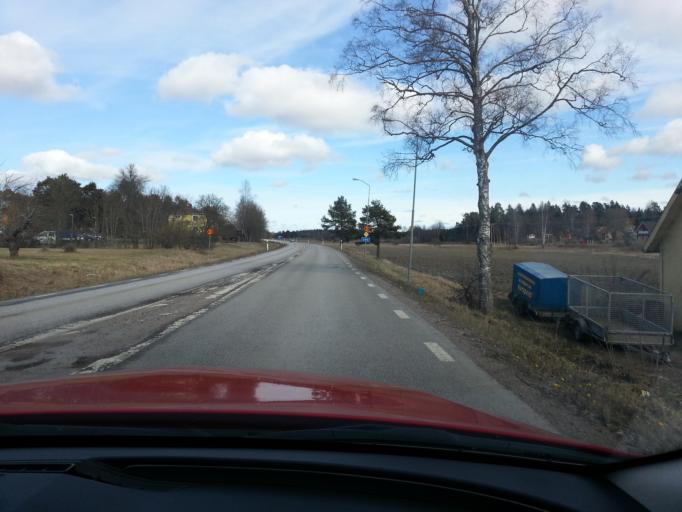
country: SE
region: Uppsala
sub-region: Osthammars Kommun
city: Gimo
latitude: 60.0631
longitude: 18.0821
